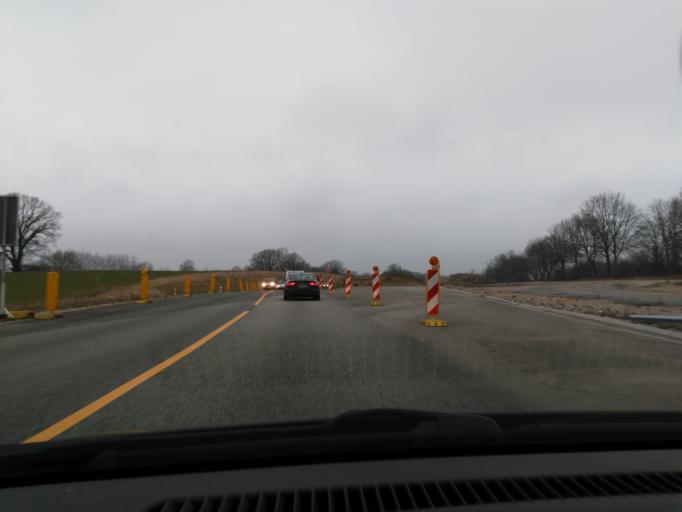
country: DE
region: Schleswig-Holstein
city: Stolpe
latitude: 54.1530
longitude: 10.2048
